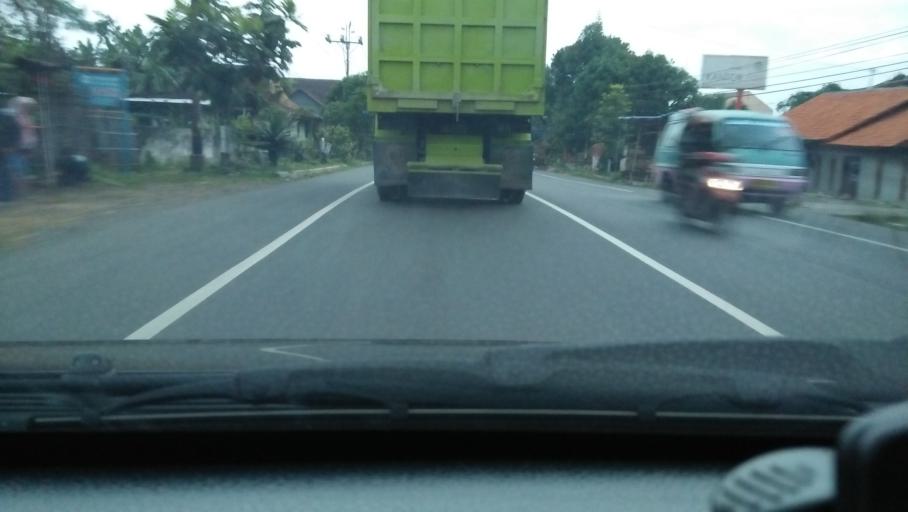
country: ID
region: Central Java
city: Magelang
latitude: -7.3899
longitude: 110.2488
